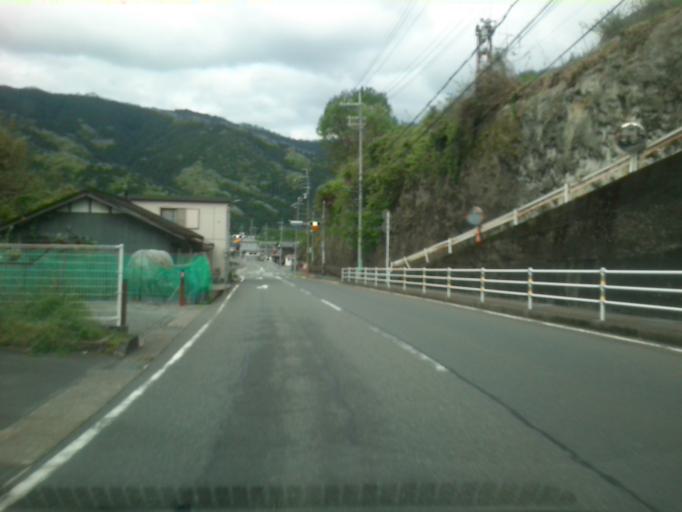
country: JP
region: Kyoto
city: Ayabe
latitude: 35.2607
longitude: 135.4044
